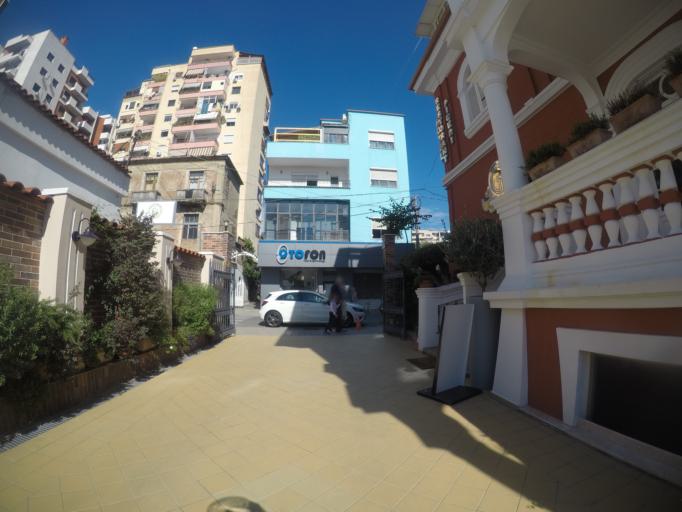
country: AL
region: Tirane
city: Tirana
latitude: 41.3305
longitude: 19.8231
